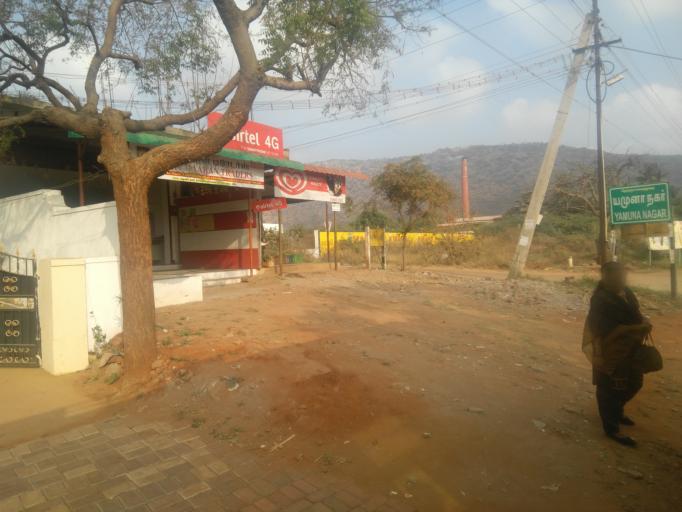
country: IN
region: Tamil Nadu
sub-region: Coimbatore
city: Perur
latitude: 11.0526
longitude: 76.8968
